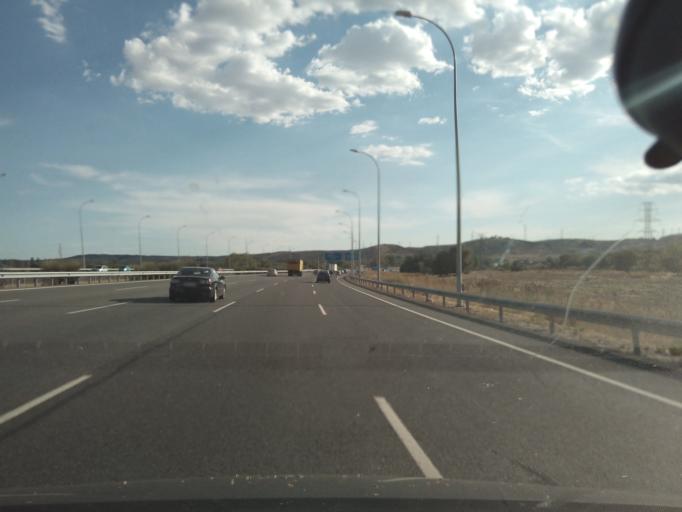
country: ES
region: Madrid
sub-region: Provincia de Madrid
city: Mejorada del Campo
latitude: 40.4165
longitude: -3.5022
